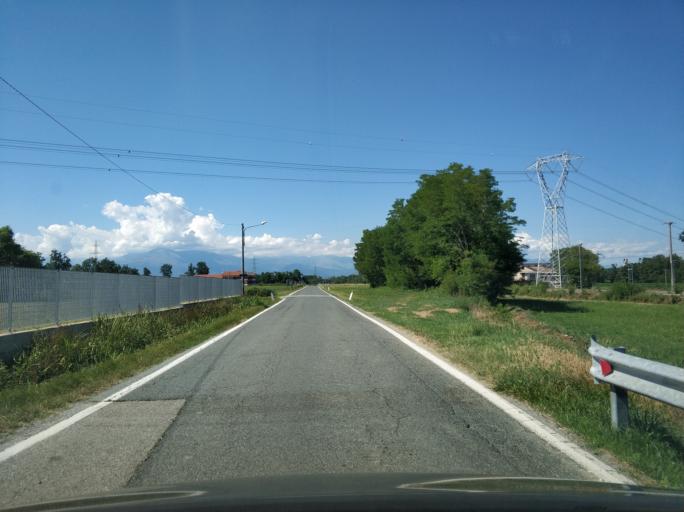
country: IT
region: Piedmont
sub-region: Provincia di Torino
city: San Benigno Canavese
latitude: 45.2378
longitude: 7.7736
